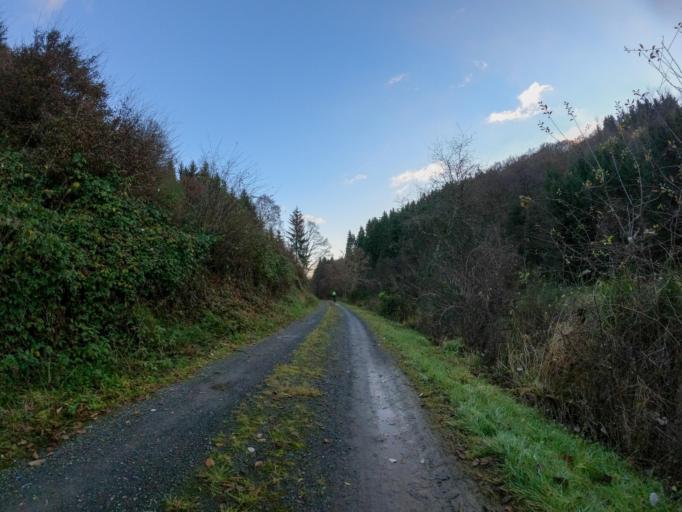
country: LU
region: Diekirch
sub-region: Canton de Wiltz
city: Bavigne
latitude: 49.9377
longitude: 5.8394
